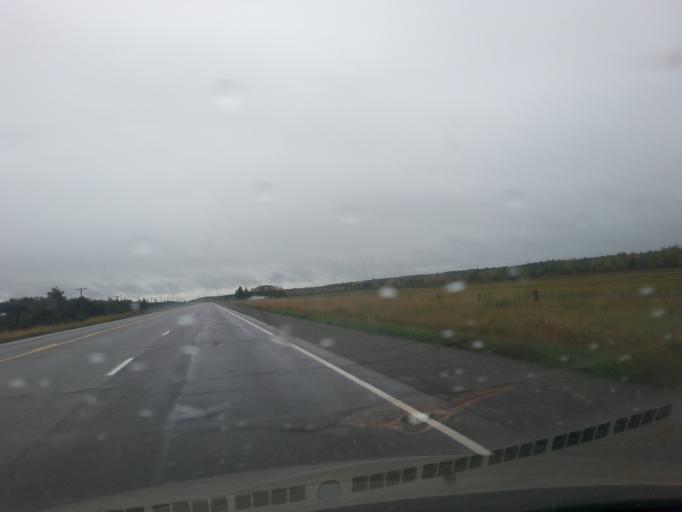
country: CA
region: Ontario
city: Greater Sudbury
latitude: 46.4325
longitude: -80.2586
